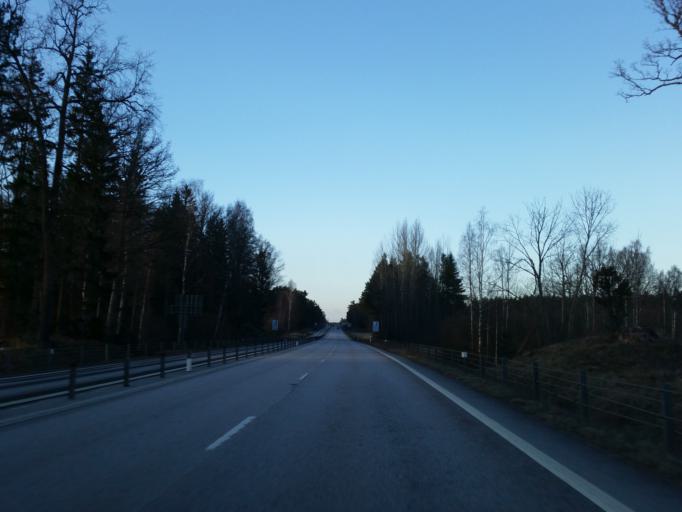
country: SE
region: Kalmar
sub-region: Oskarshamns Kommun
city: Oskarshamn
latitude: 57.3442
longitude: 16.4884
